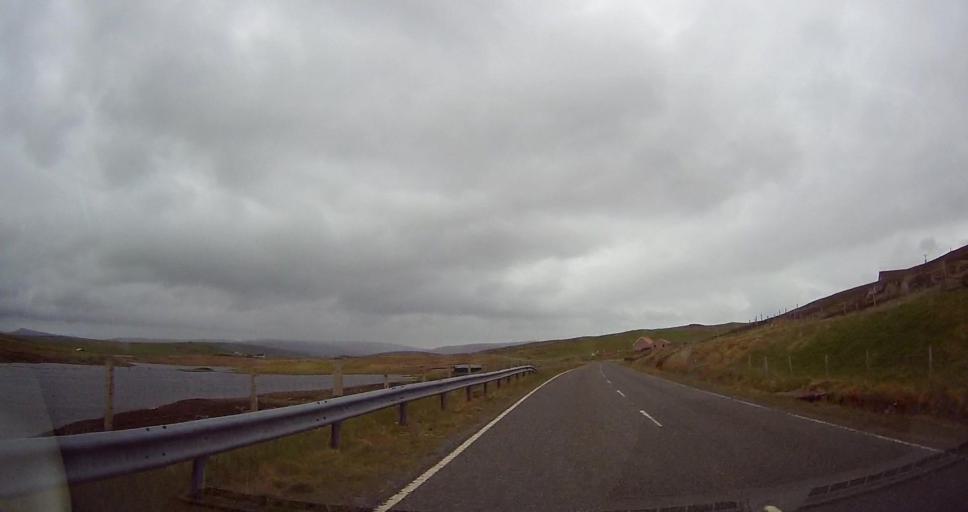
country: GB
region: Scotland
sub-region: Shetland Islands
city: Lerwick
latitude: 60.2568
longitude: -1.4690
